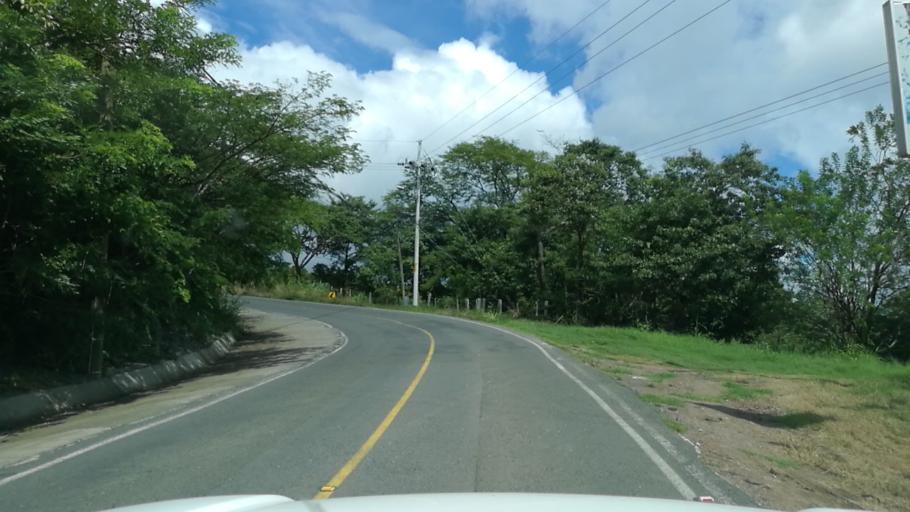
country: CR
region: Guanacaste
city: Bagaces
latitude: 10.5378
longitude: -85.2553
